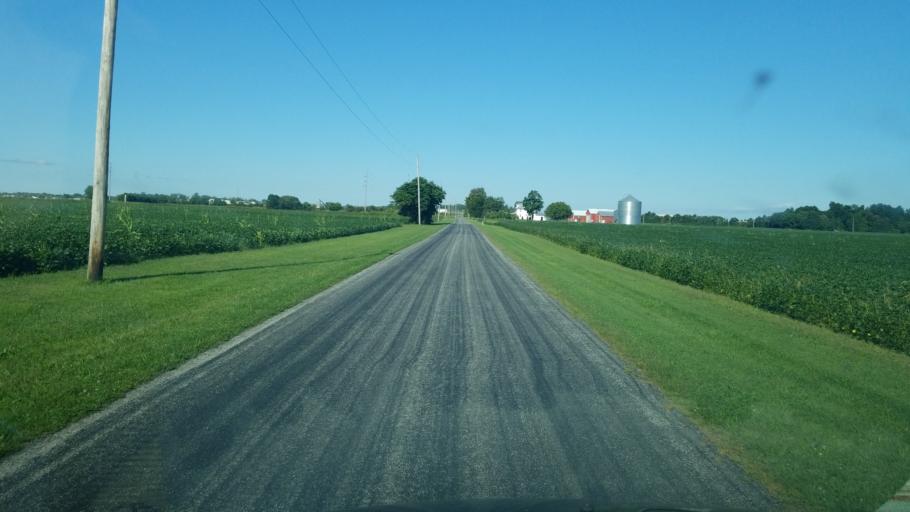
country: US
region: Ohio
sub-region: Wyandot County
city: Carey
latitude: 40.9719
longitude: -83.3441
